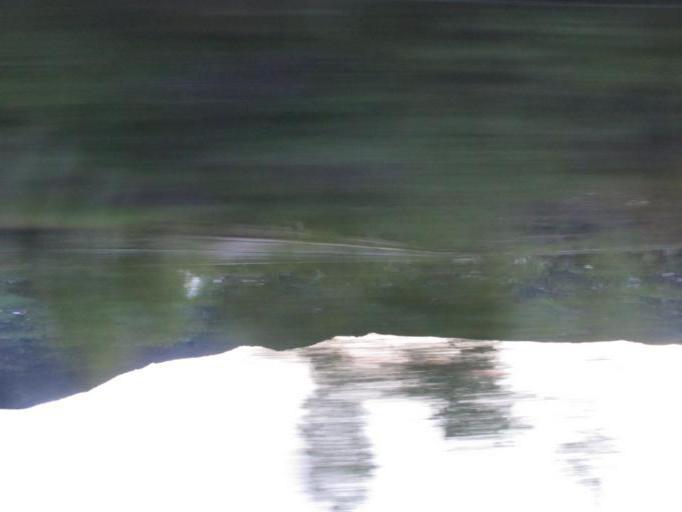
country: NO
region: Oppland
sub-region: Ringebu
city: Ringebu
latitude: 61.4504
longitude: 10.1847
